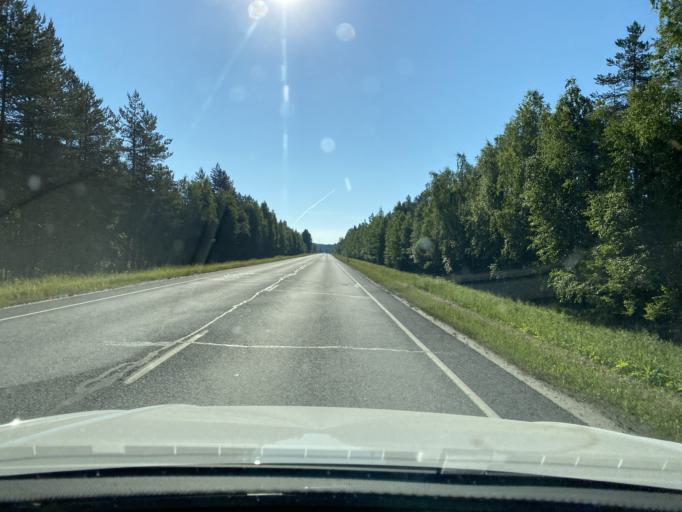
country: FI
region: Haeme
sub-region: Forssa
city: Tammela
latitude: 60.8265
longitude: 23.9401
